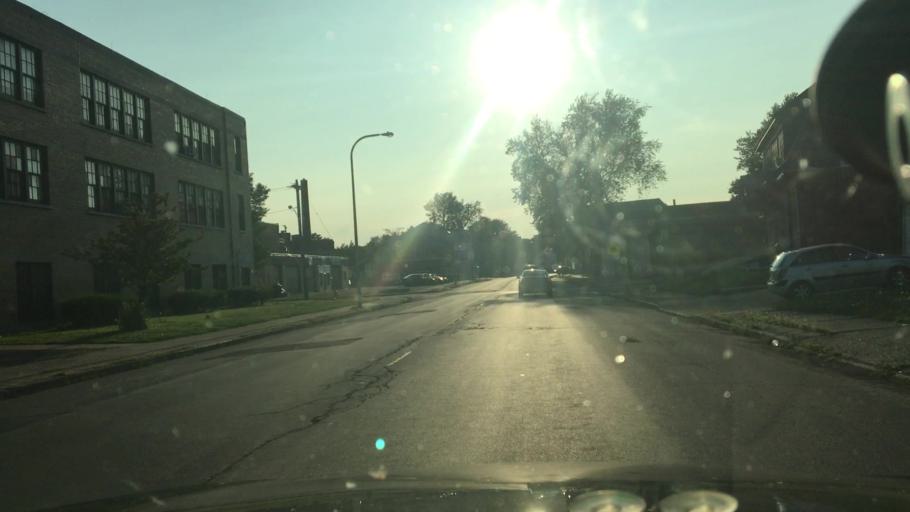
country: US
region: New York
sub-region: Erie County
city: West Seneca
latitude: 42.8566
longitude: -78.8266
